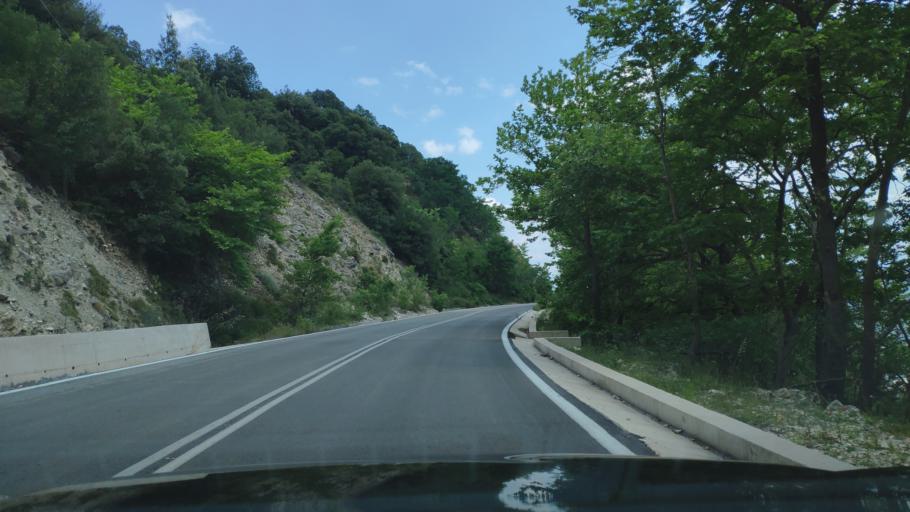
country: GR
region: Epirus
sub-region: Nomos Artas
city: Agios Dimitrios
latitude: 39.3472
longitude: 21.0055
